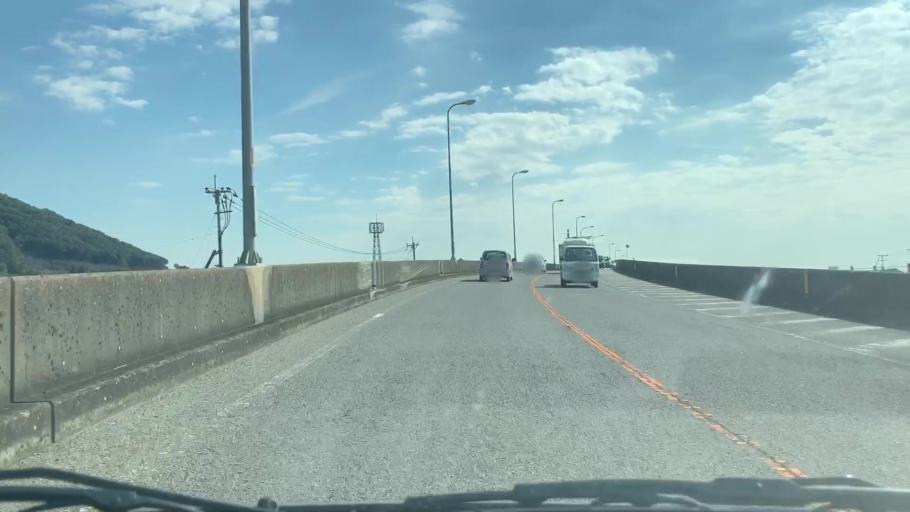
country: JP
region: Saga Prefecture
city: Kashima
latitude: 33.2208
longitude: 130.1511
